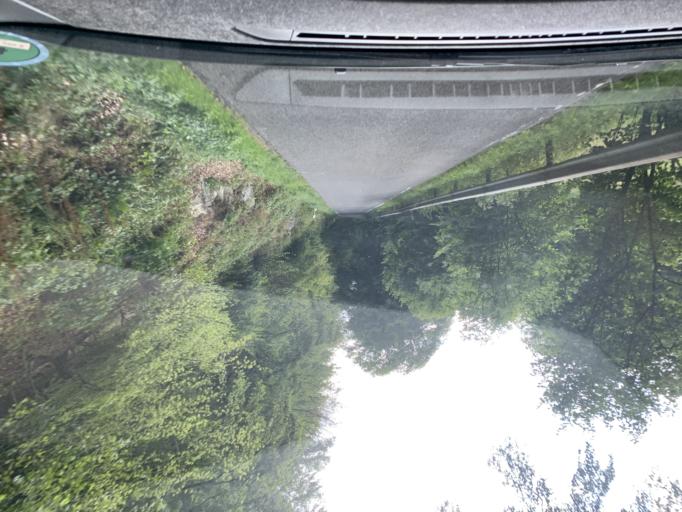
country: DE
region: North Rhine-Westphalia
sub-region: Regierungsbezirk Koln
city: Hurtgenwald
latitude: 50.6608
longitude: 6.3475
